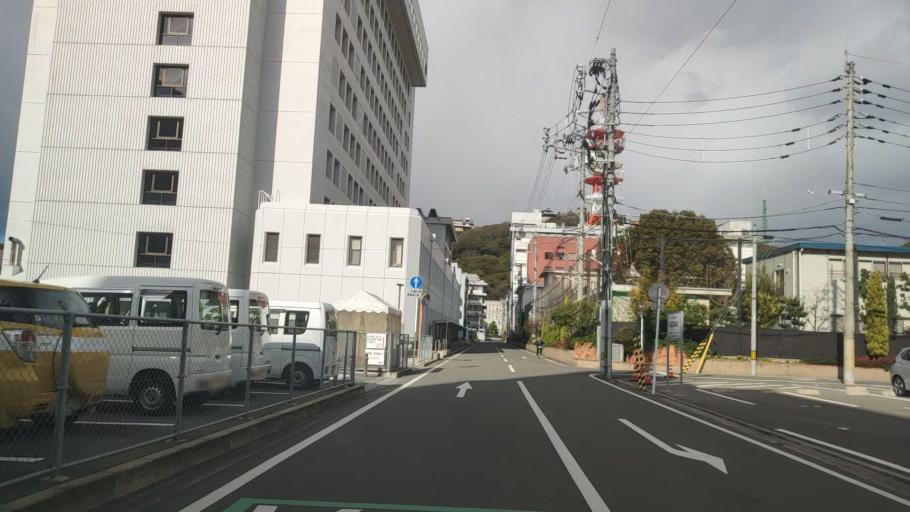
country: JP
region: Ehime
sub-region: Shikoku-chuo Shi
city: Matsuyama
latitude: 33.8385
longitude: 132.7658
